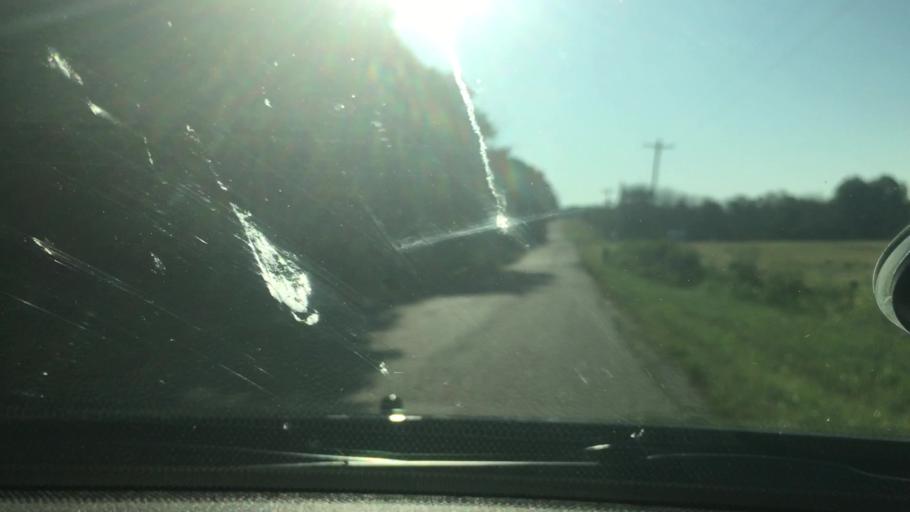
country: US
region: Oklahoma
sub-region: Murray County
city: Sulphur
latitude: 34.4049
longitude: -96.8018
